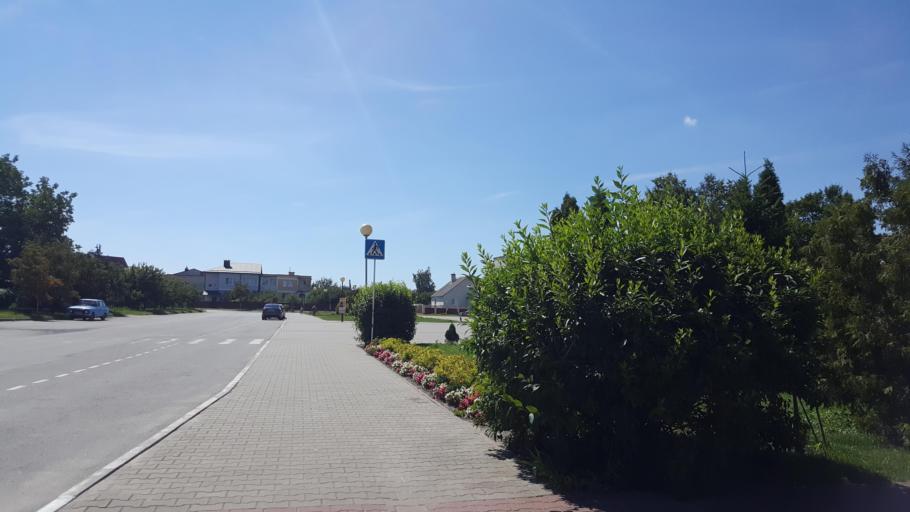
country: BY
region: Brest
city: Charnawchytsy
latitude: 52.2665
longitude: 23.5886
